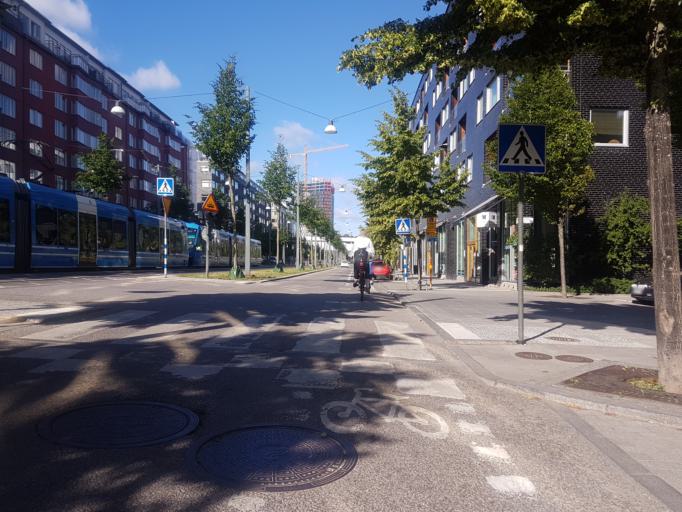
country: SE
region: Stockholm
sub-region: Stockholms Kommun
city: OEstermalm
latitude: 59.3046
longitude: 18.0939
